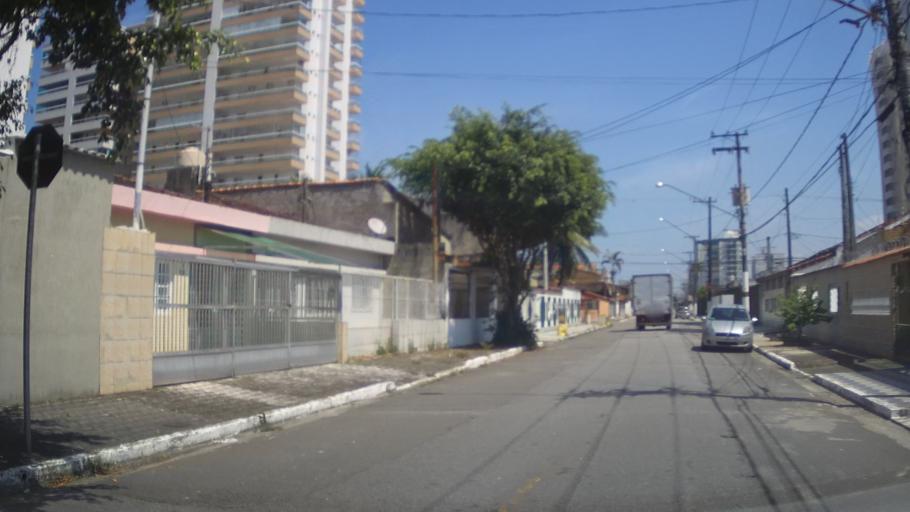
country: BR
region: Sao Paulo
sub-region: Praia Grande
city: Praia Grande
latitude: -24.0083
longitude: -46.4272
